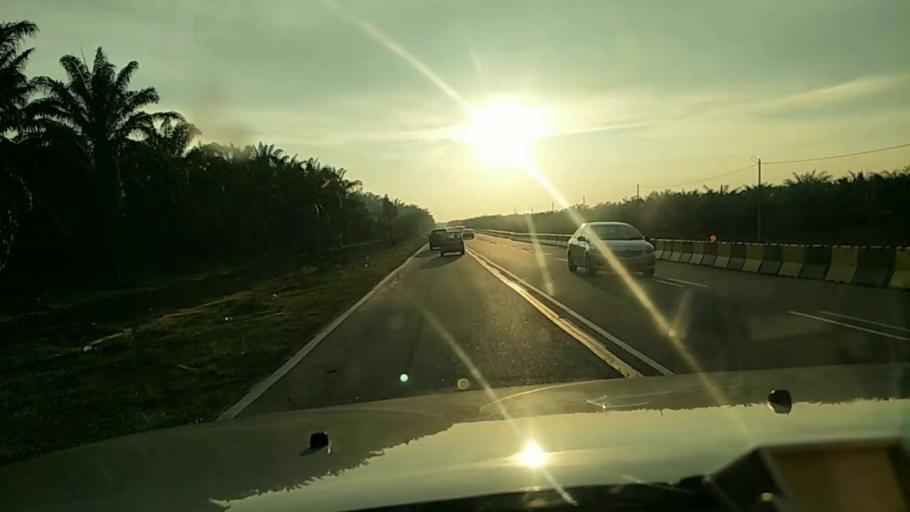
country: MY
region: Perak
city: Kampong Dungun
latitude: 3.3072
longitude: 101.3388
